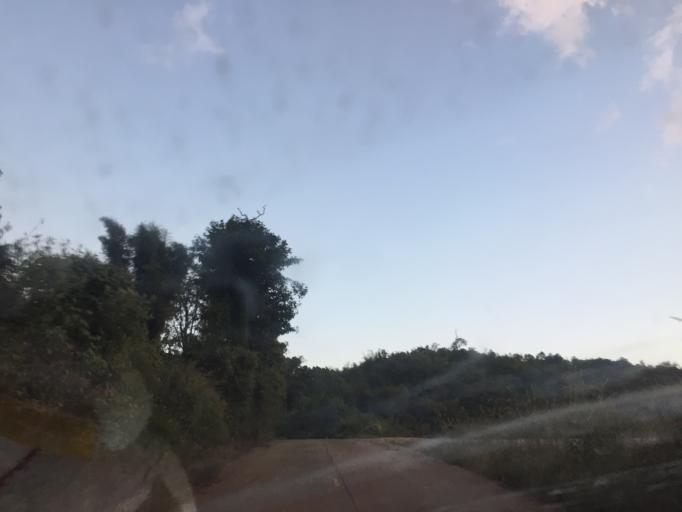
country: TH
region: Chiang Mai
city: Samoeng
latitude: 19.0039
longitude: 98.7115
